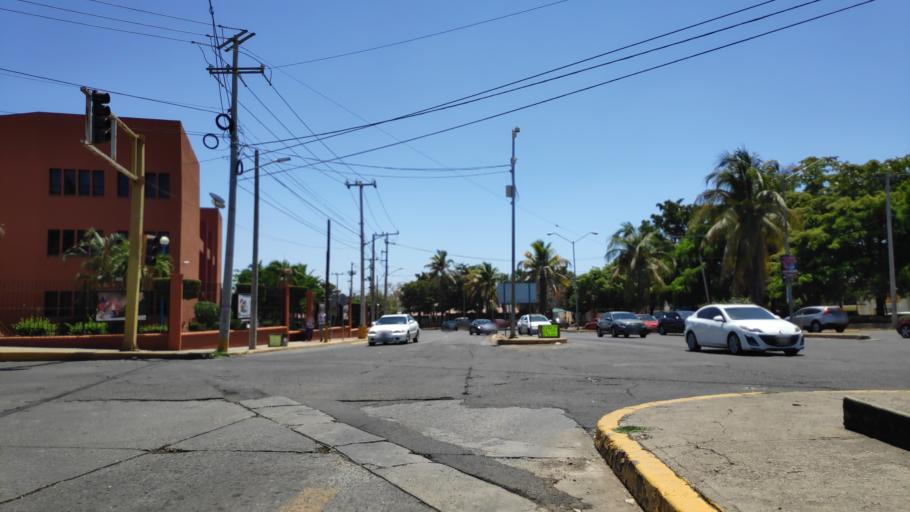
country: MX
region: Sinaloa
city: Culiacan
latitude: 24.8221
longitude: -107.3833
